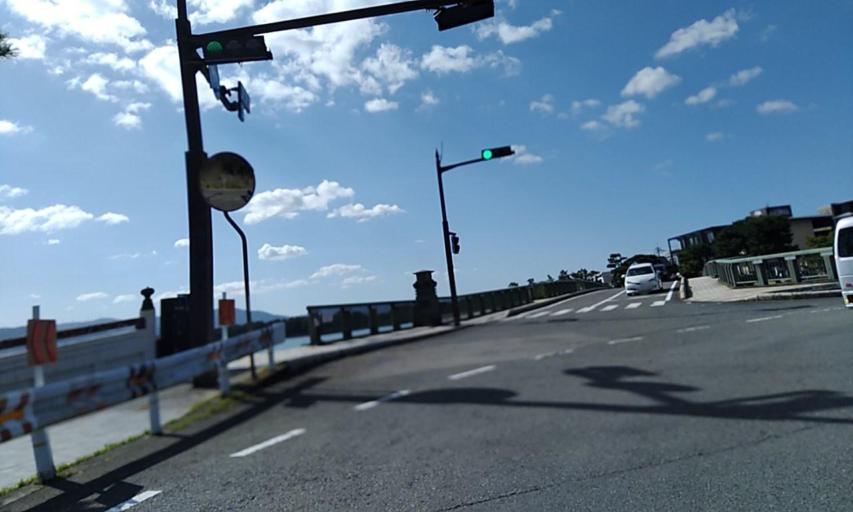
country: JP
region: Wakayama
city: Minato
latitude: 34.1871
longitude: 135.1733
